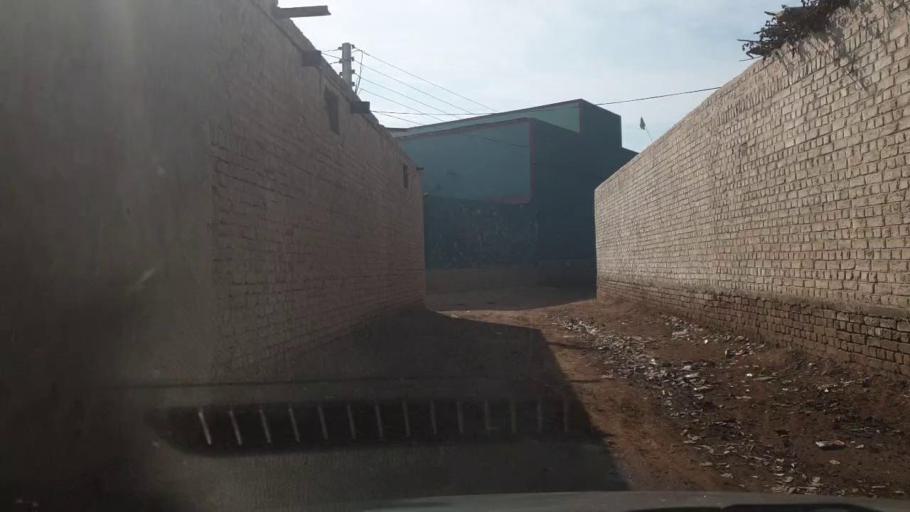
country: PK
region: Sindh
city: Shahpur Chakar
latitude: 26.1731
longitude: 68.5840
